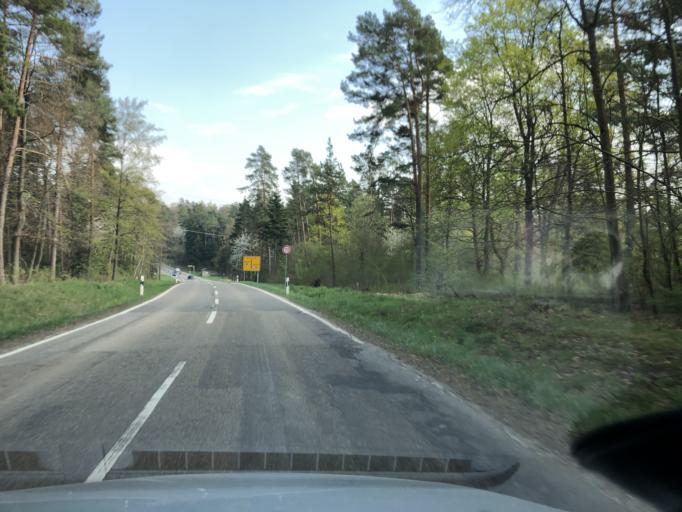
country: DE
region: Baden-Wuerttemberg
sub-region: Karlsruhe Region
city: Simmozheim
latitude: 48.7617
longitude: 8.8216
